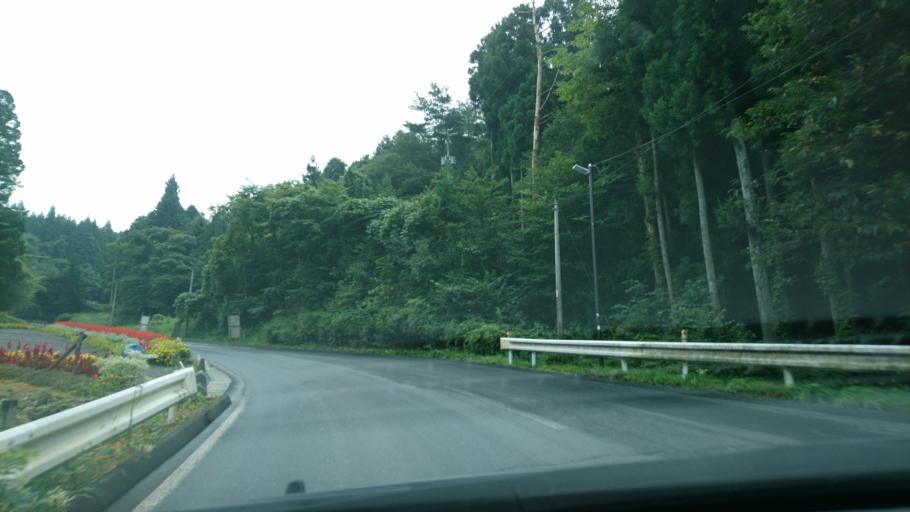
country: JP
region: Iwate
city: Ichinoseki
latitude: 38.9387
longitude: 141.1803
